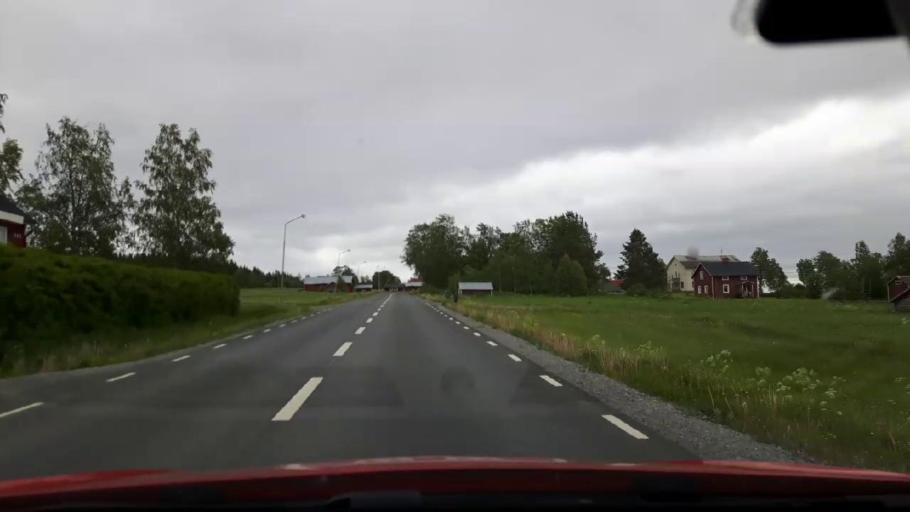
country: SE
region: Jaemtland
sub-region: OEstersunds Kommun
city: Lit
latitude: 63.7405
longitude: 14.8573
